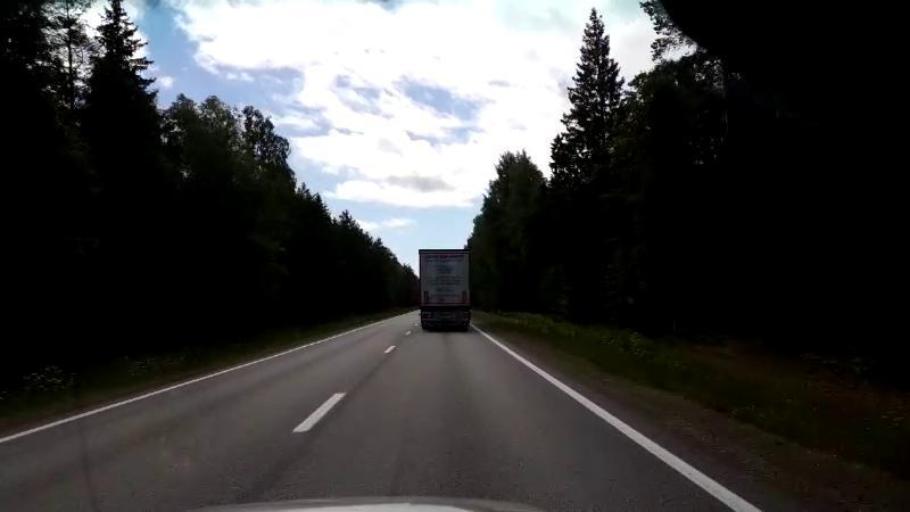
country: LV
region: Salacgrivas
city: Salacgriva
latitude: 57.5239
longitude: 24.4308
